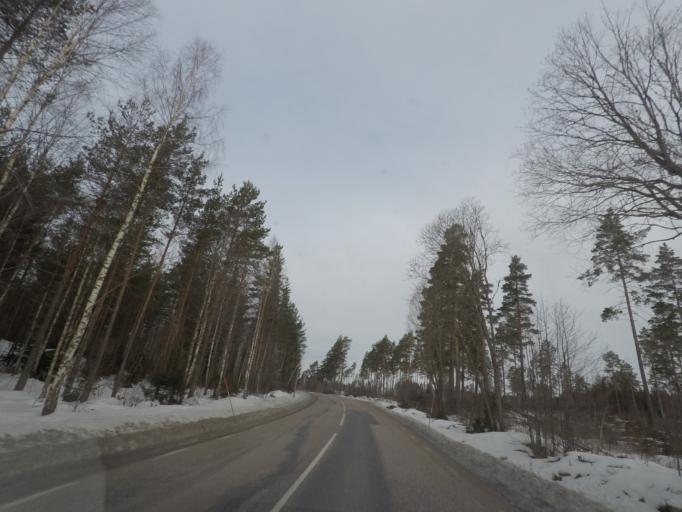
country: SE
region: Vaestmanland
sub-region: Vasteras
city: Skultuna
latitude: 59.7520
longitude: 16.3221
